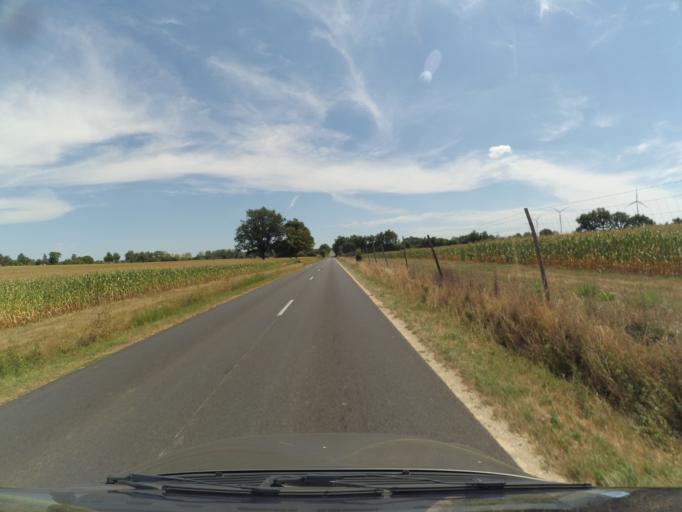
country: FR
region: Poitou-Charentes
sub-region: Departement de la Vienne
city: Saint-Maurice-la-Clouere
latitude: 46.3617
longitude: 0.4330
